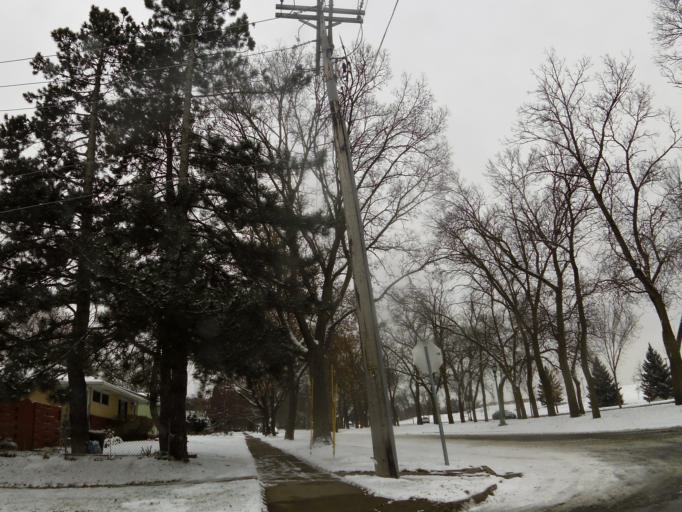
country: US
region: Minnesota
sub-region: Ramsey County
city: Maplewood
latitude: 44.9740
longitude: -93.0439
